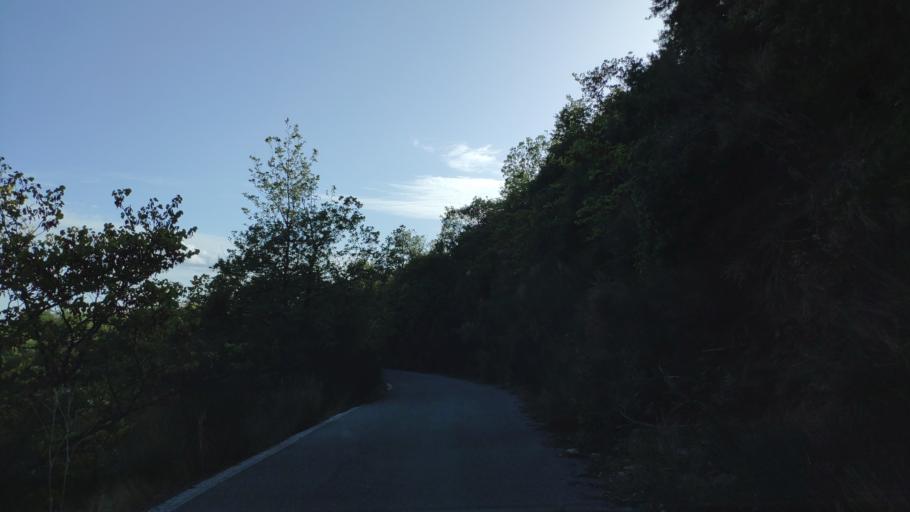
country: GR
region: Peloponnese
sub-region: Nomos Arkadias
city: Dimitsana
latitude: 37.5539
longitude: 22.0411
